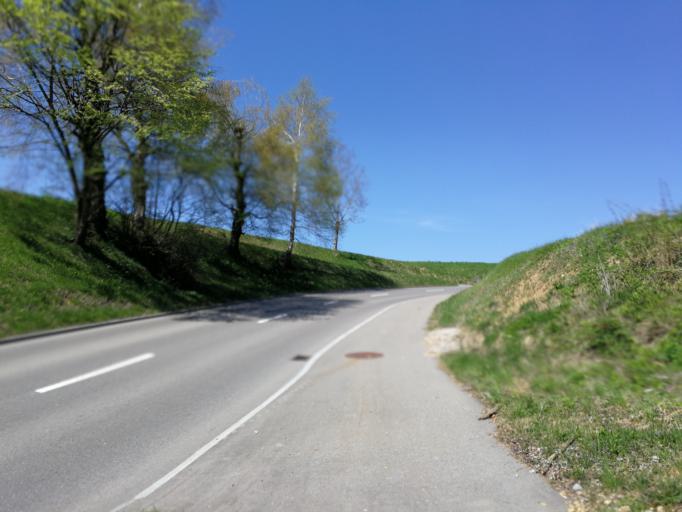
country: CH
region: Zurich
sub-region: Bezirk Meilen
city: Herrliberg
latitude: 47.2971
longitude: 8.6329
